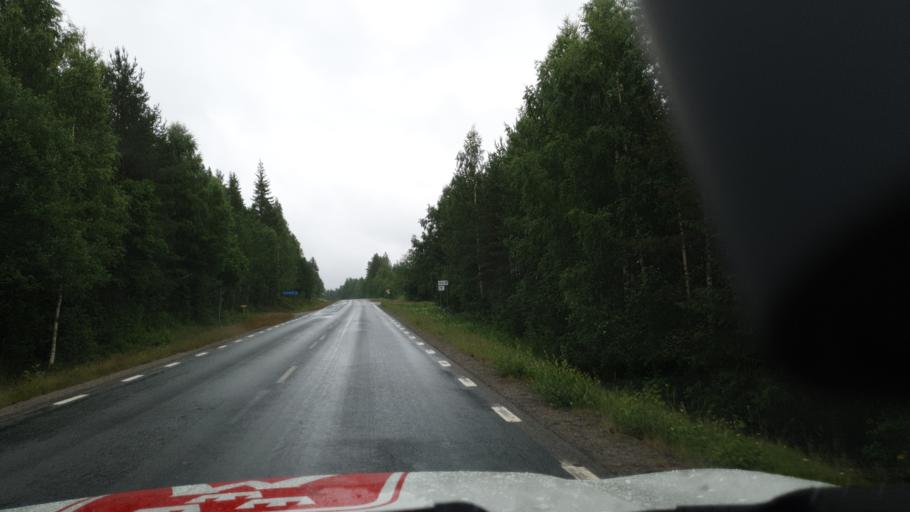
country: SE
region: Vaesterbotten
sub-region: Vannas Kommun
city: Vaennaes
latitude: 63.7715
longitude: 19.7001
